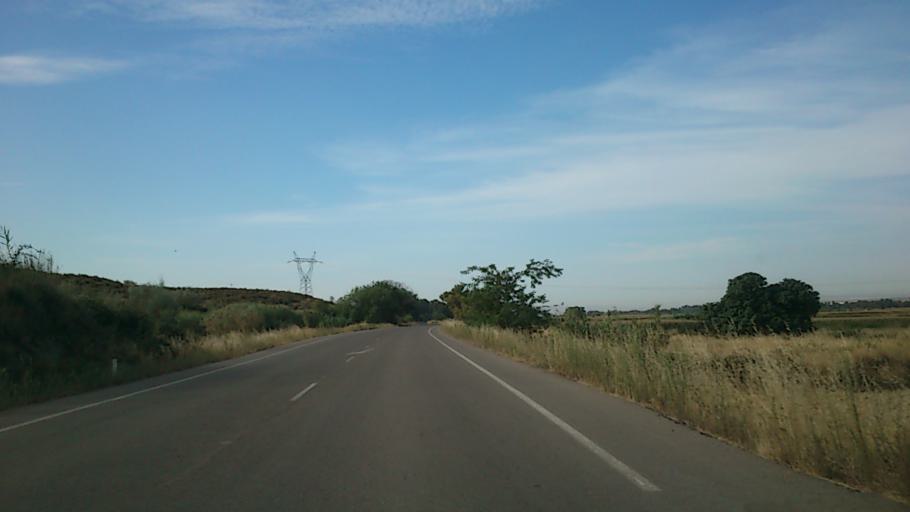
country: ES
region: Aragon
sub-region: Provincia de Zaragoza
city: San Mateo de Gallego
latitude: 41.7951
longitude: -0.7814
